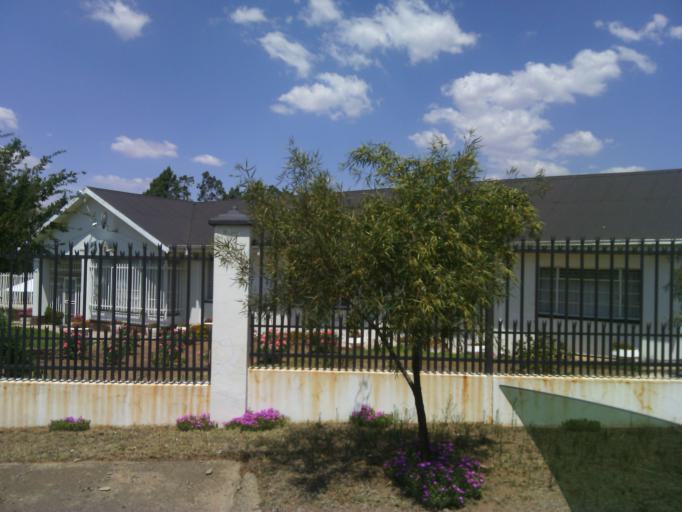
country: ZA
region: Orange Free State
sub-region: Xhariep District Municipality
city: Dewetsdorp
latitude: -29.5804
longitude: 26.6625
